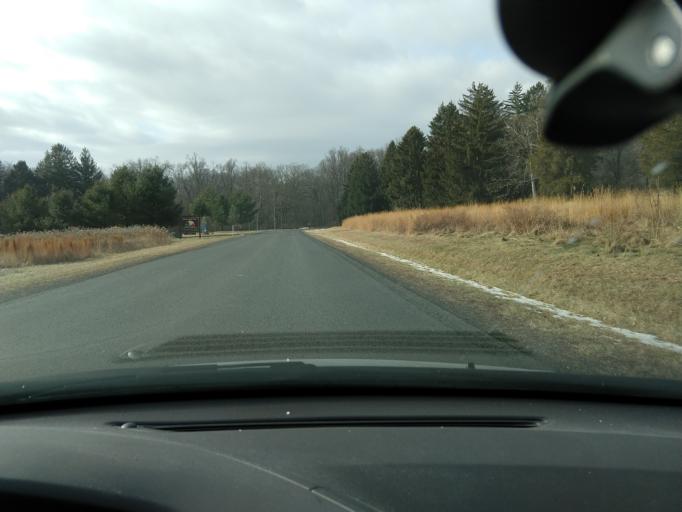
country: US
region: Pennsylvania
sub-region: Chester County
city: Elverson
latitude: 40.1992
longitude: -75.7927
